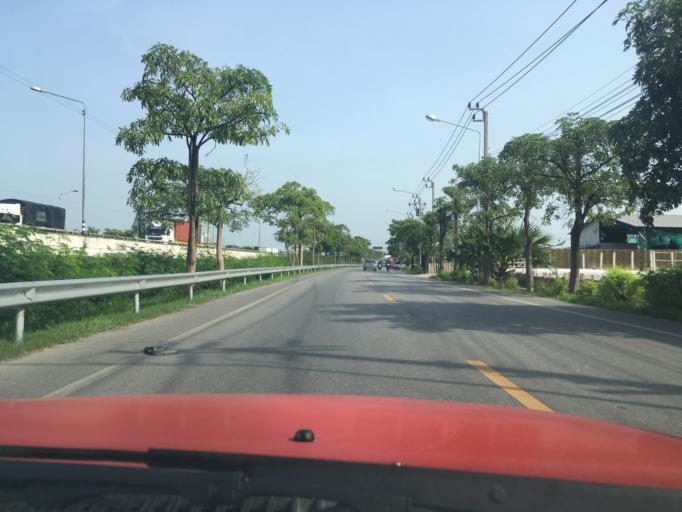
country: TH
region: Bangkok
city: Bang Khun Thian
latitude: 13.6309
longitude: 100.4178
